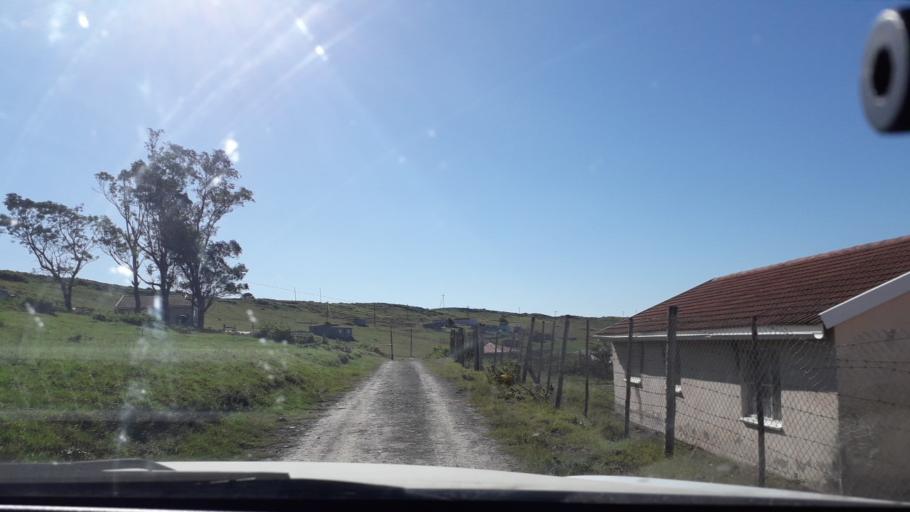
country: ZA
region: Eastern Cape
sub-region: Buffalo City Metropolitan Municipality
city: East London
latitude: -32.8420
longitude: 27.9928
